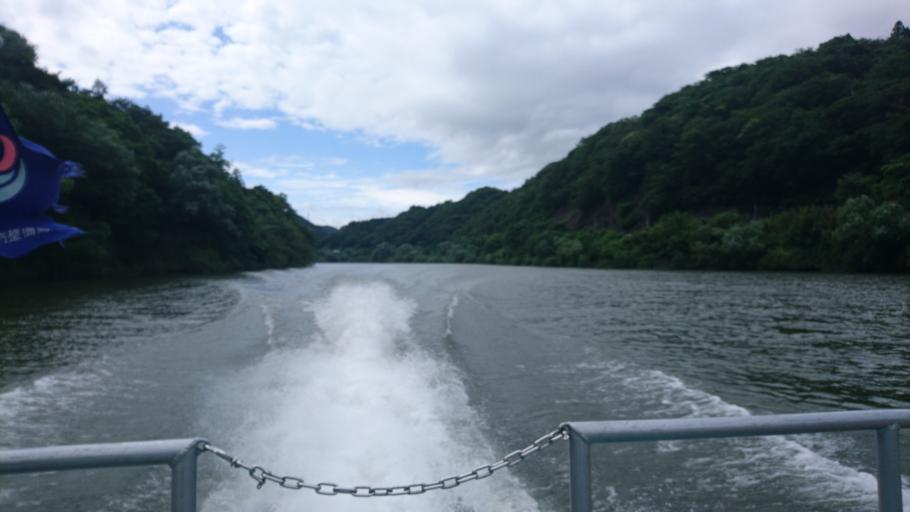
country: JP
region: Iwate
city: Ichinoseki
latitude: 38.9060
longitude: 141.2465
